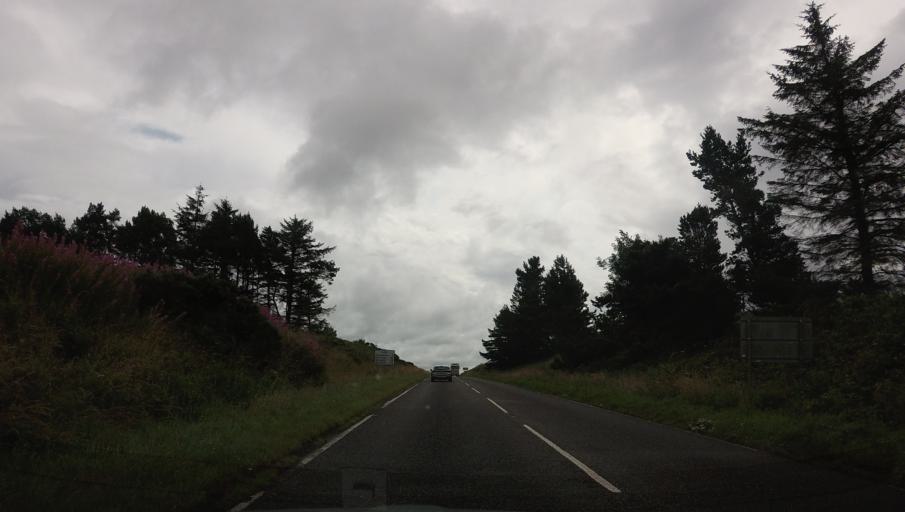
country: GB
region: Scotland
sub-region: Aberdeenshire
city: Stonehaven
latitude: 56.9475
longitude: -2.2196
